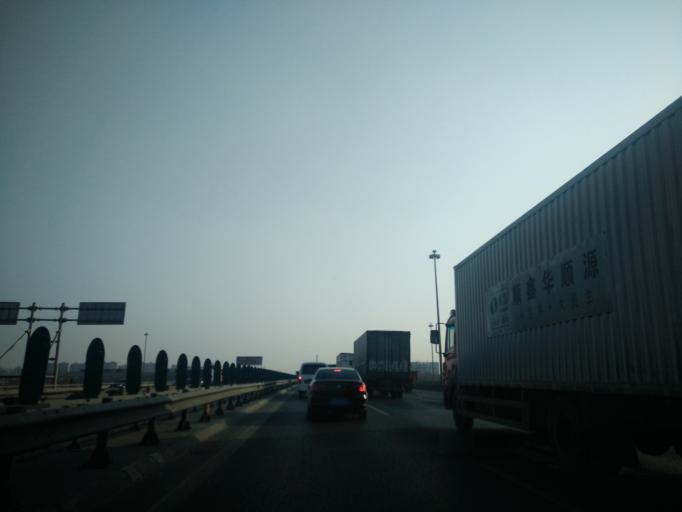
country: CN
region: Beijing
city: Dongfeng
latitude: 39.8693
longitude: 116.5426
